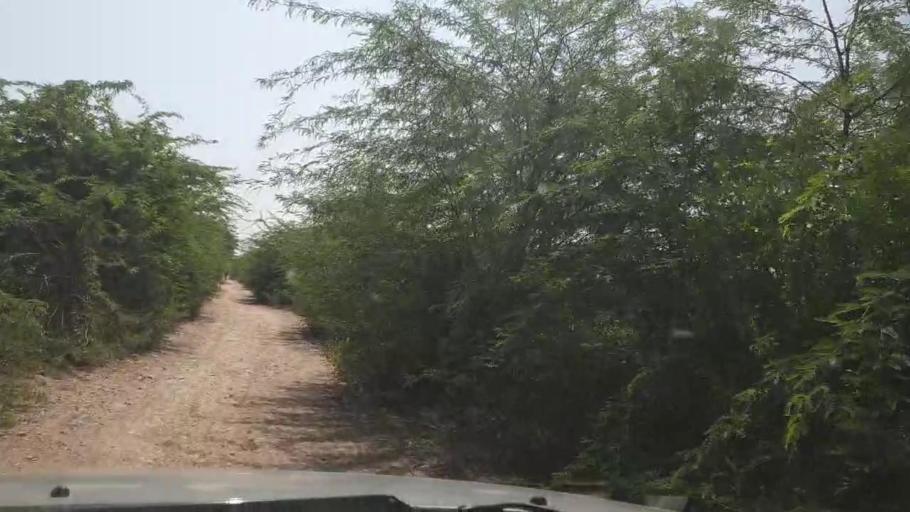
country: PK
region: Sindh
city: Tando Ghulam Ali
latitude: 25.1136
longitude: 68.8101
